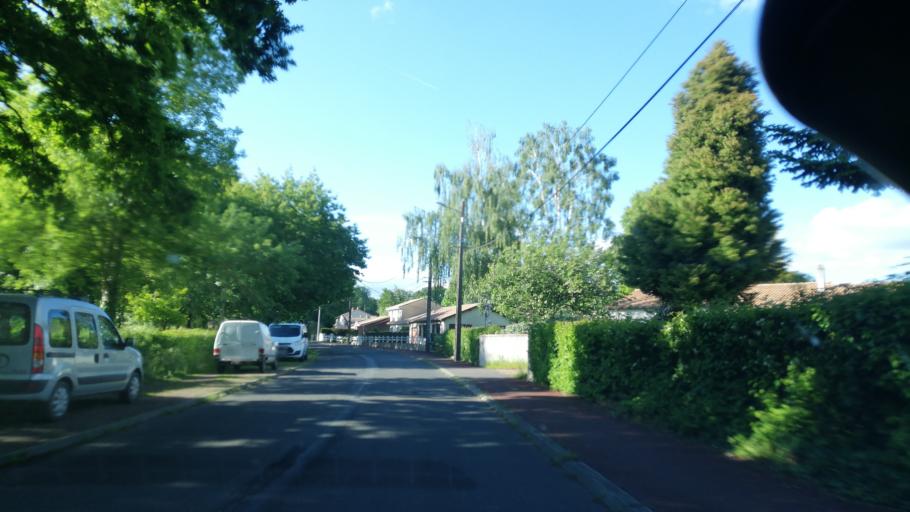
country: FR
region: Poitou-Charentes
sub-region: Departement des Deux-Sevres
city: Boisme
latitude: 46.7758
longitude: -0.4329
